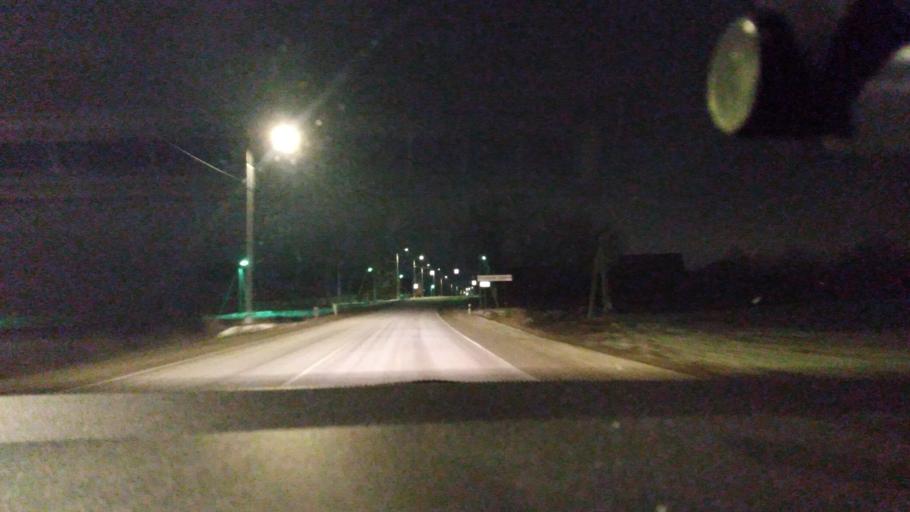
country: RU
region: Moskovskaya
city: Lukhovitsy
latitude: 55.0940
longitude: 38.9570
